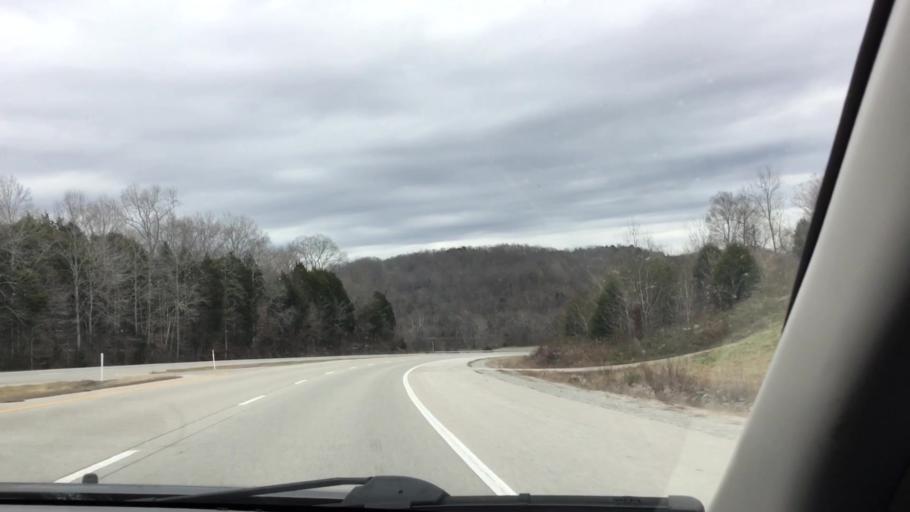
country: US
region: Tennessee
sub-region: Lewis County
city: Hohenwald
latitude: 35.5923
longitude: -87.4552
